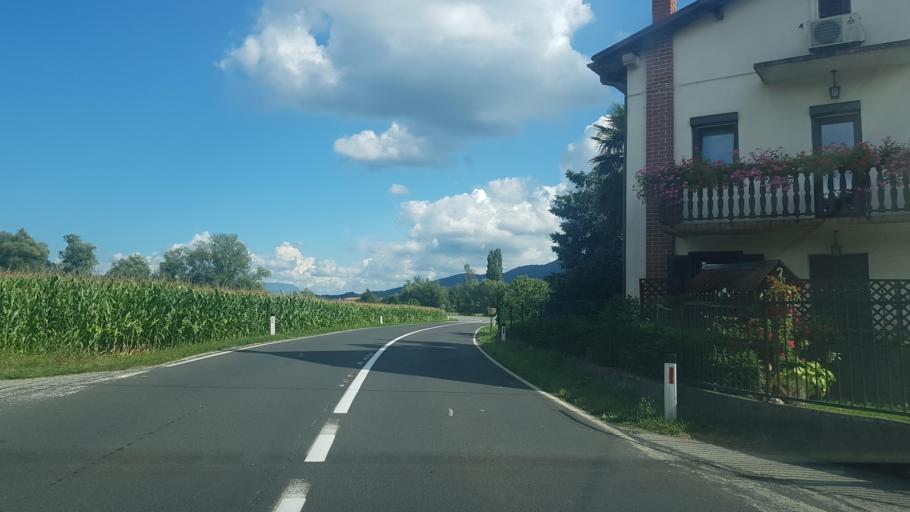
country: SI
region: Rence-Vogrsko
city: Volcja Draga
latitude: 45.9005
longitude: 13.6809
